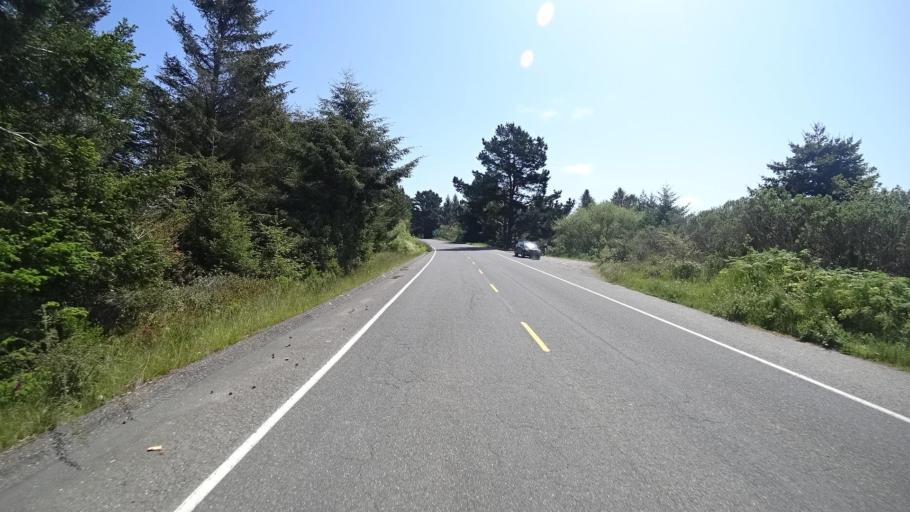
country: US
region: California
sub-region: Humboldt County
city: Fortuna
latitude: 40.6425
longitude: -124.2117
